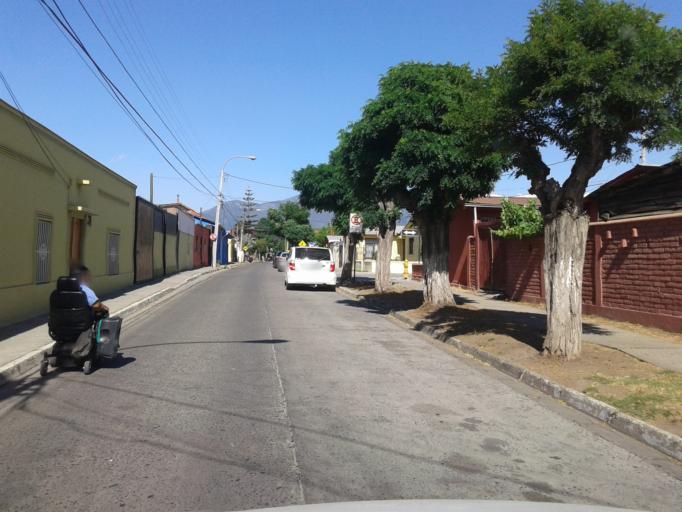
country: CL
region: Valparaiso
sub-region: Provincia de Quillota
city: Quillota
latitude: -32.8780
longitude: -71.2566
